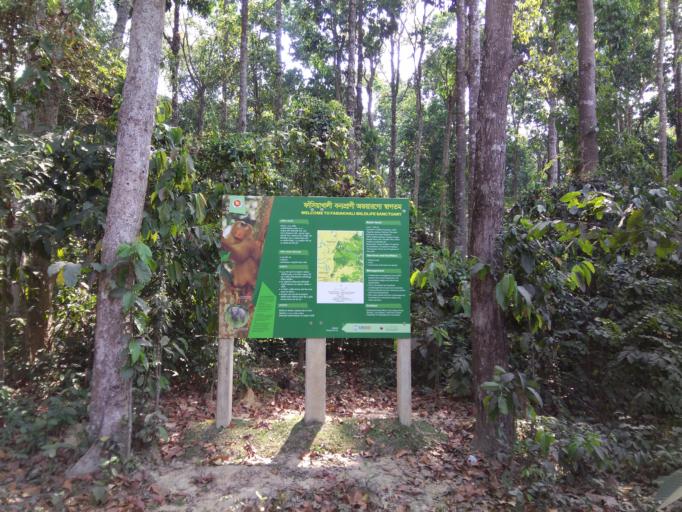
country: BD
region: Chittagong
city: Cox's Bazar
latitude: 21.7154
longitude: 92.0832
